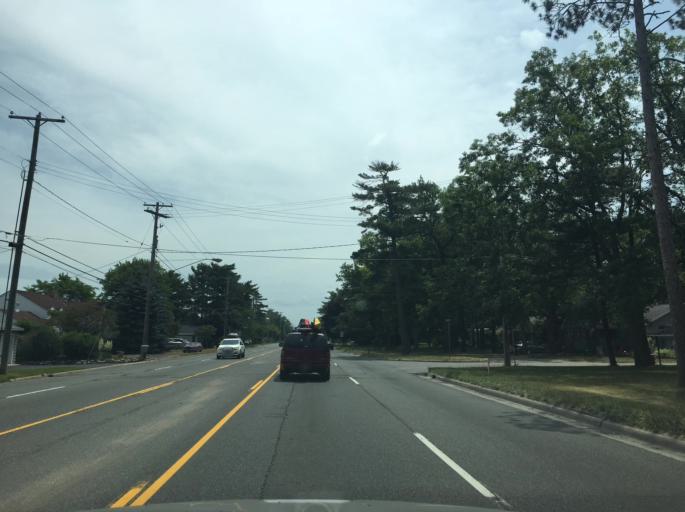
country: US
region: Michigan
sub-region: Grand Traverse County
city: Traverse City
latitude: 44.7534
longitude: -85.5692
